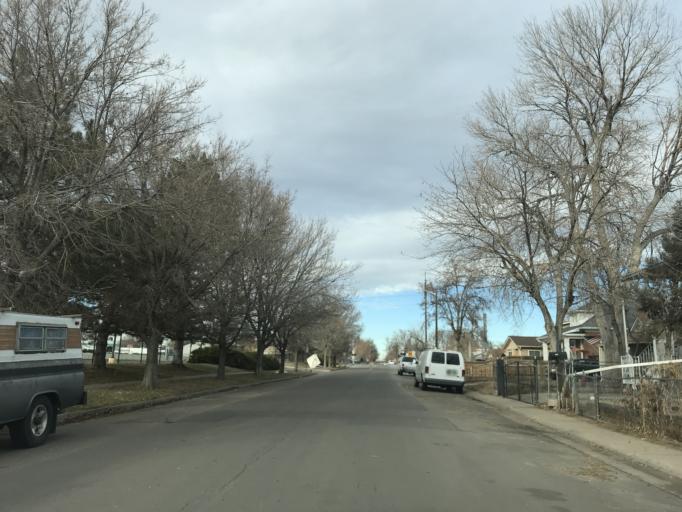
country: US
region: Colorado
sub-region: Adams County
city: Commerce City
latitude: 39.7740
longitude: -104.9542
